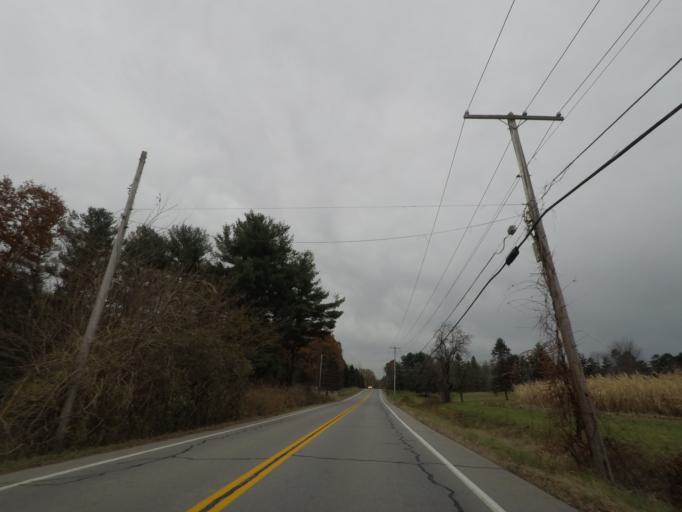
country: US
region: New York
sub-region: Schenectady County
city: Niskayuna
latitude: 42.8183
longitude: -73.8261
